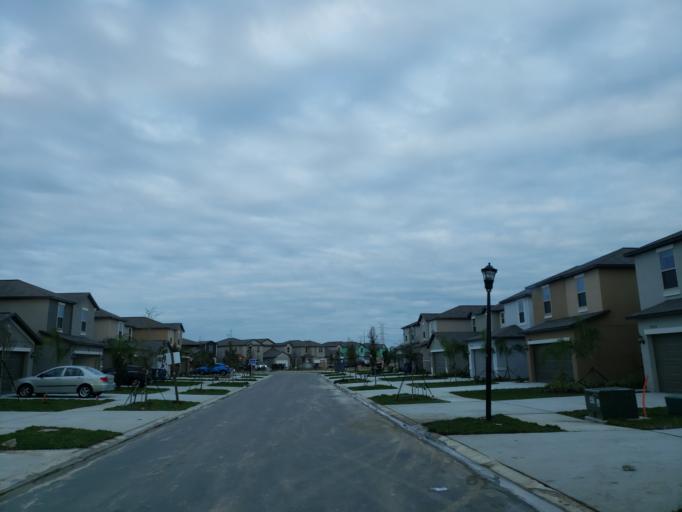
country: US
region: Florida
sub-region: Hillsborough County
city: Progress Village
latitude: 27.9086
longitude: -82.3733
